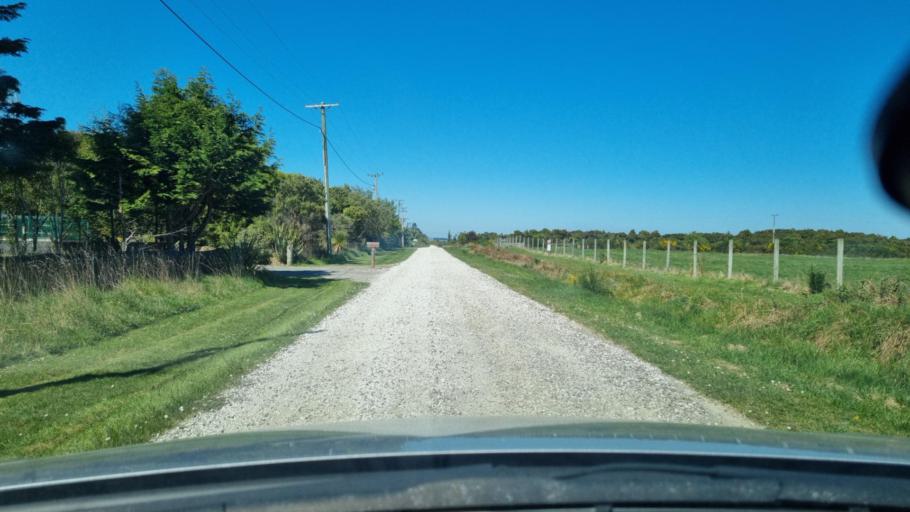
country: NZ
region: Southland
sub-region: Invercargill City
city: Invercargill
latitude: -46.4495
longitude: 168.3166
